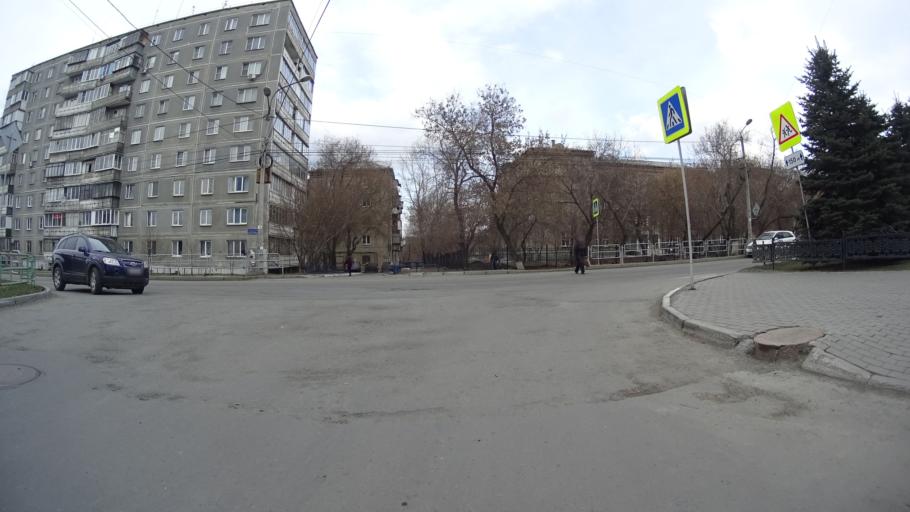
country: RU
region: Chelyabinsk
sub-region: Gorod Chelyabinsk
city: Chelyabinsk
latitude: 55.1628
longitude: 61.4212
